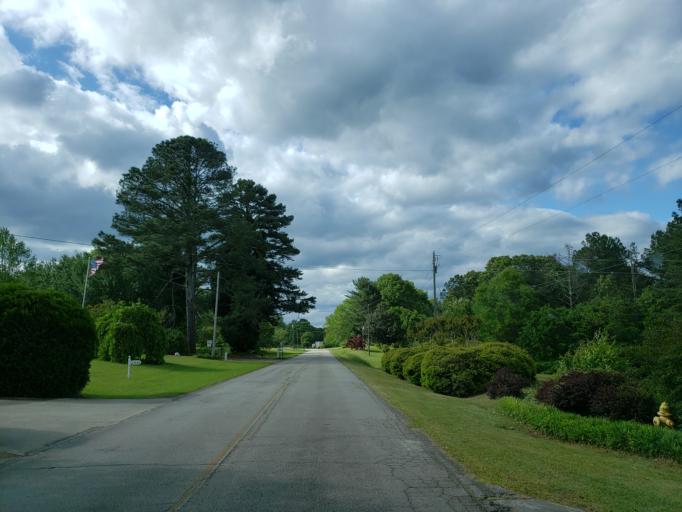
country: US
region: Georgia
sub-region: Haralson County
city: Tallapoosa
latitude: 33.6921
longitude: -85.3028
